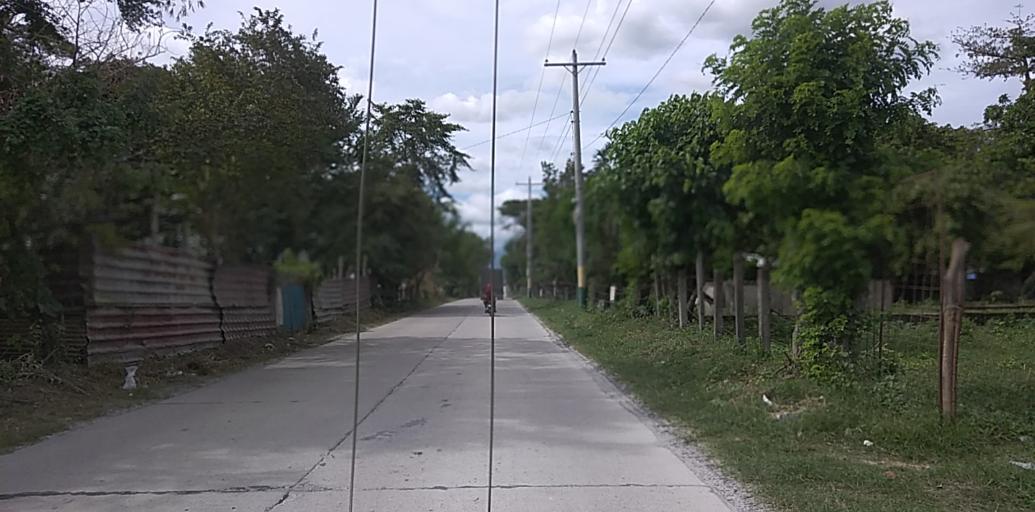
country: PH
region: Central Luzon
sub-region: Province of Pampanga
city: Pulung Santol
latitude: 15.0672
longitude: 120.5640
